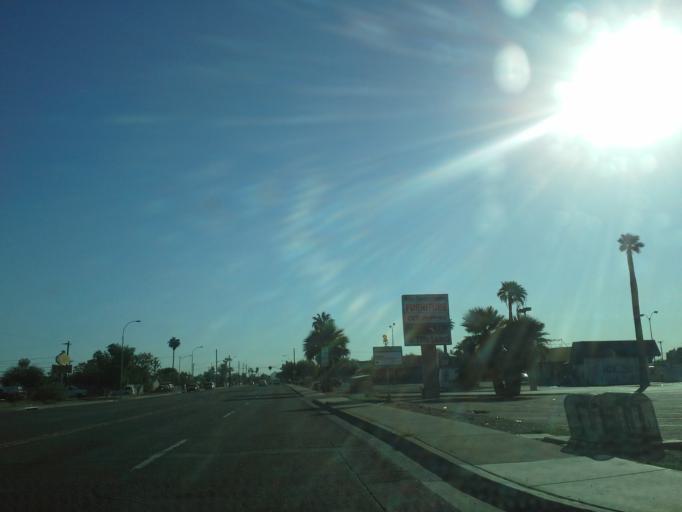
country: US
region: Arizona
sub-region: Maricopa County
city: Glendale
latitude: 33.4804
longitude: -112.1509
